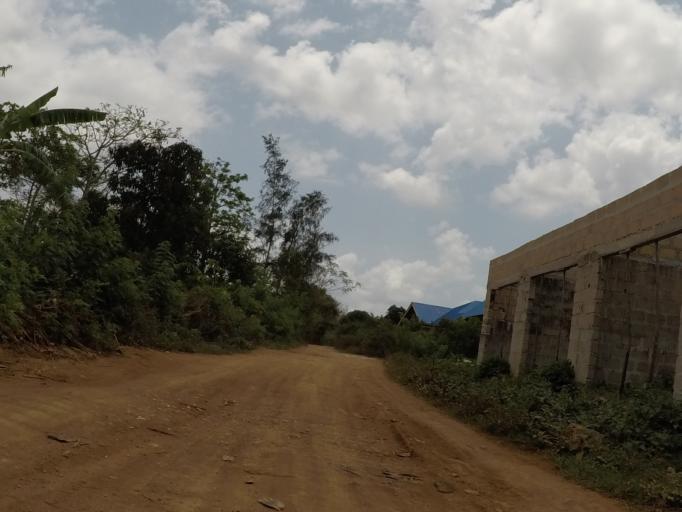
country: TZ
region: Zanzibar Central/South
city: Koani
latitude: -6.1866
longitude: 39.3095
